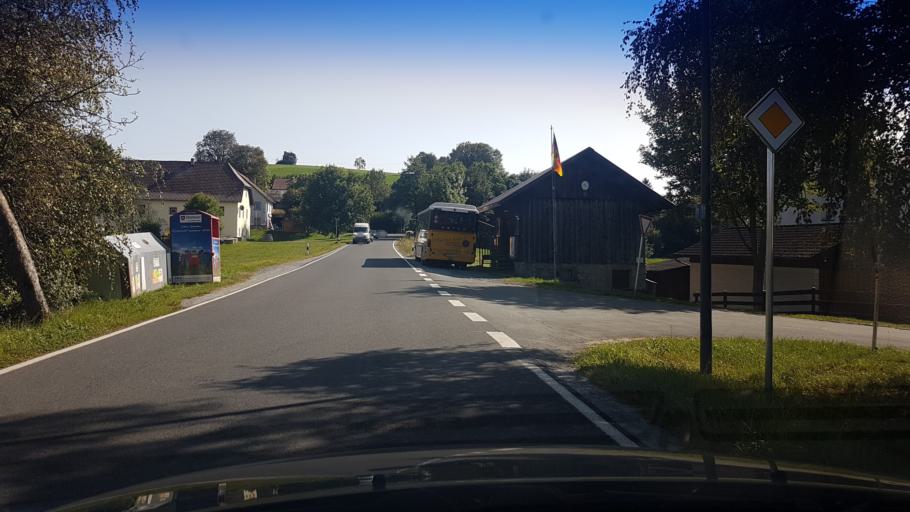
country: DE
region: Bavaria
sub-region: Upper Franconia
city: Marktschorgast
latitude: 50.0761
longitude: 11.6724
